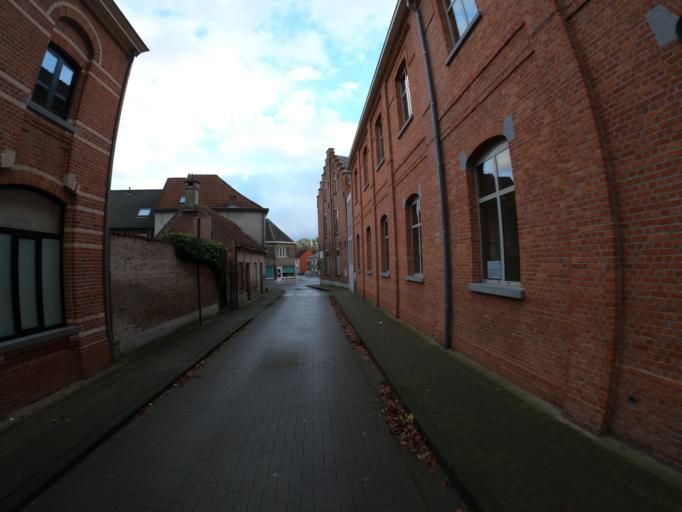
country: BE
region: Flanders
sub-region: Provincie Oost-Vlaanderen
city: Hamme
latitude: 51.1117
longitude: 4.1741
